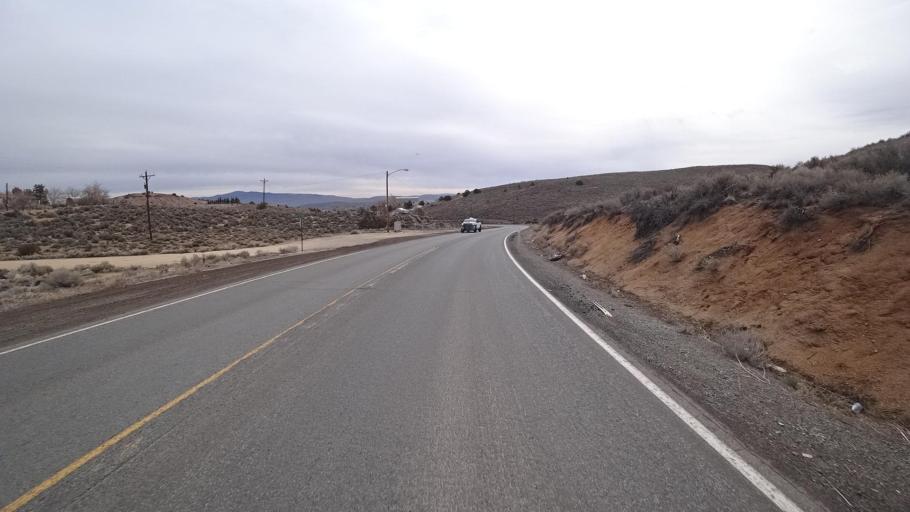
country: US
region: Nevada
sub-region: Washoe County
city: Sun Valley
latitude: 39.6009
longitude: -119.8015
